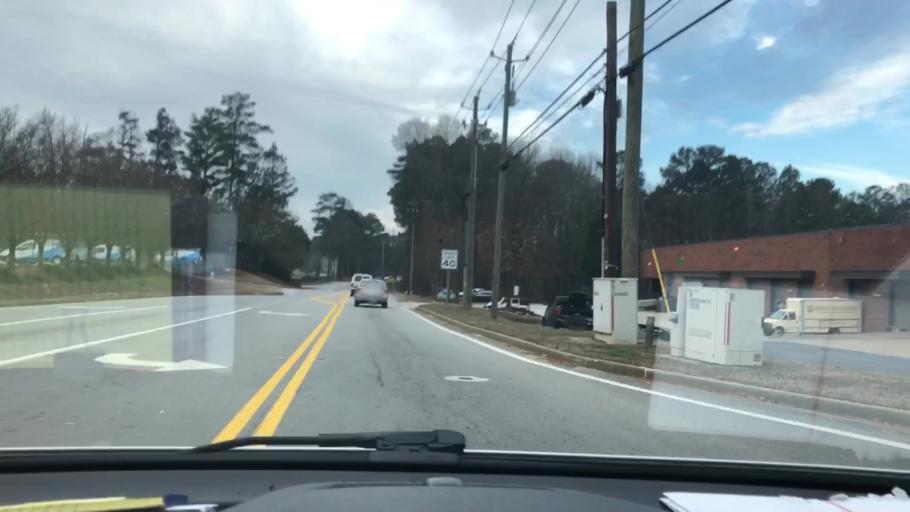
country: US
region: Georgia
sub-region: Gwinnett County
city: Berkeley Lake
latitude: 33.9689
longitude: -84.1817
